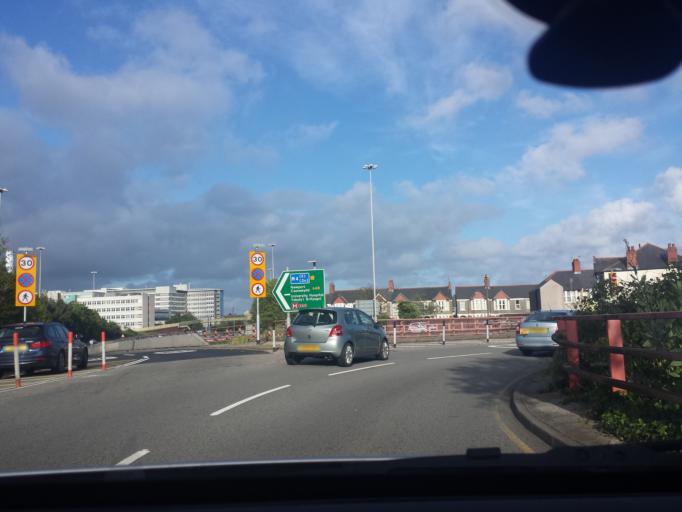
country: GB
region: Wales
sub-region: Cardiff
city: Cardiff
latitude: 51.5052
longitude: -3.1979
